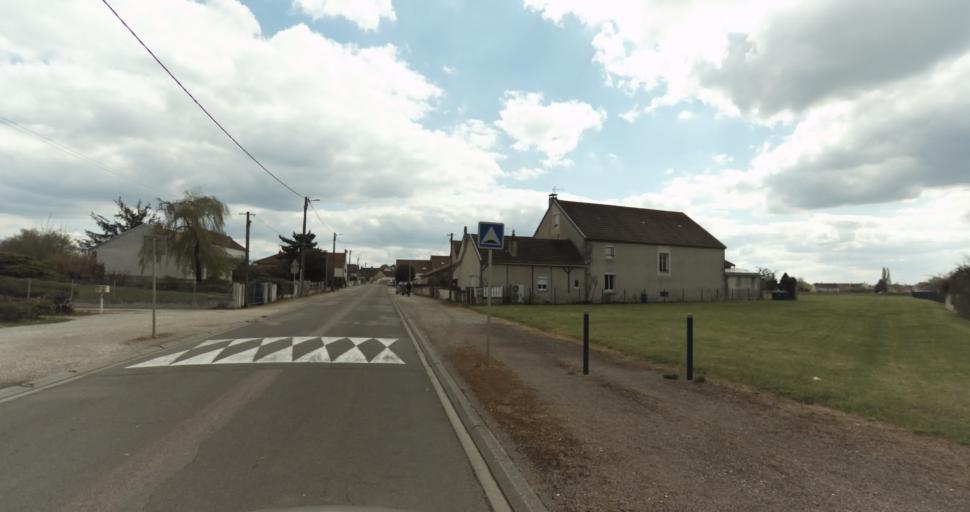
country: FR
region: Bourgogne
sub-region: Departement de la Cote-d'Or
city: Auxonne
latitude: 47.1879
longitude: 5.3905
